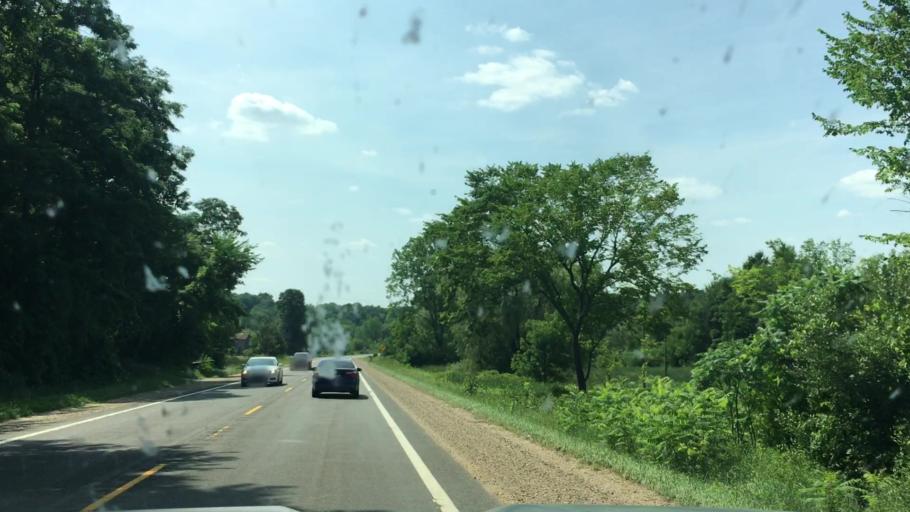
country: US
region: Michigan
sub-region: Allegan County
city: Plainwell
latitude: 42.4360
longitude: -85.5735
